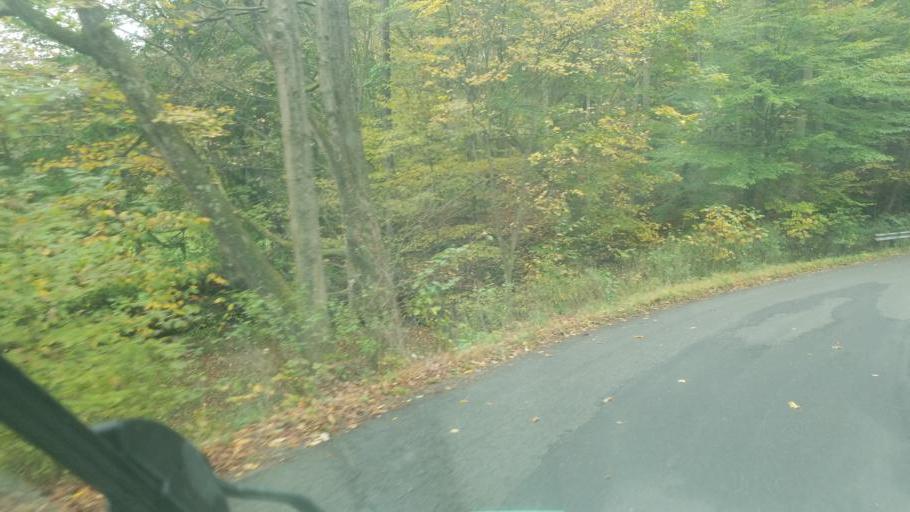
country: US
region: Ohio
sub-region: Holmes County
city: Millersburg
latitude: 40.5698
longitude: -81.8683
